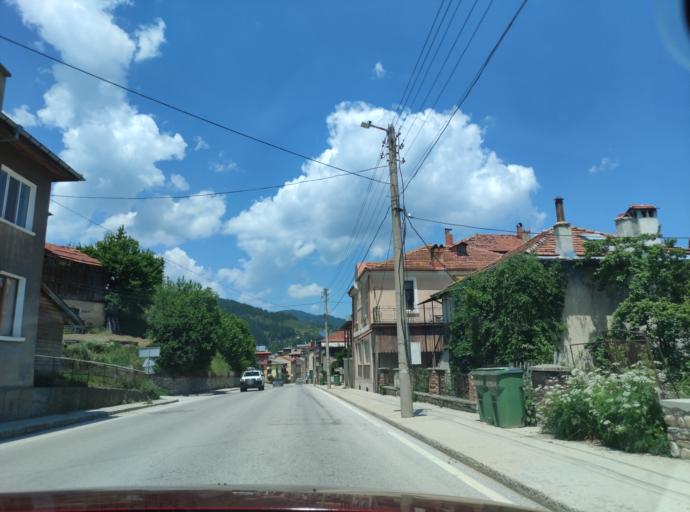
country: BG
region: Smolyan
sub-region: Obshtina Chepelare
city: Chepelare
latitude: 41.7207
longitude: 24.6865
